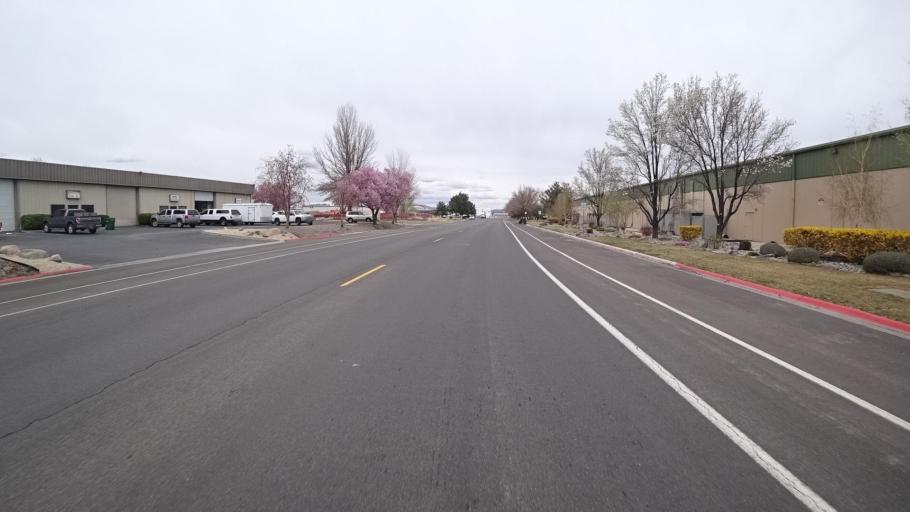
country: US
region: Nevada
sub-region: Washoe County
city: Sparks
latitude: 39.5180
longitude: -119.7370
